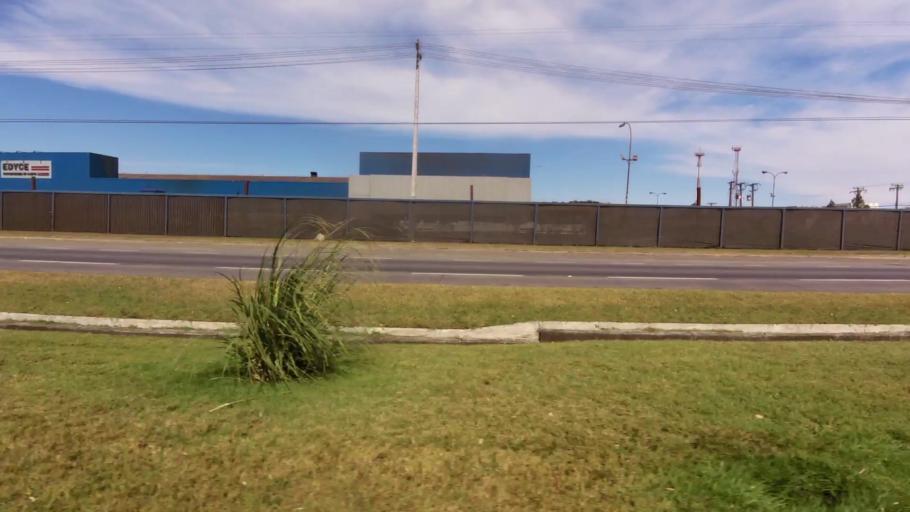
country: CL
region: Biobio
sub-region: Provincia de Concepcion
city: Talcahuano
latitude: -36.7560
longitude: -73.1227
